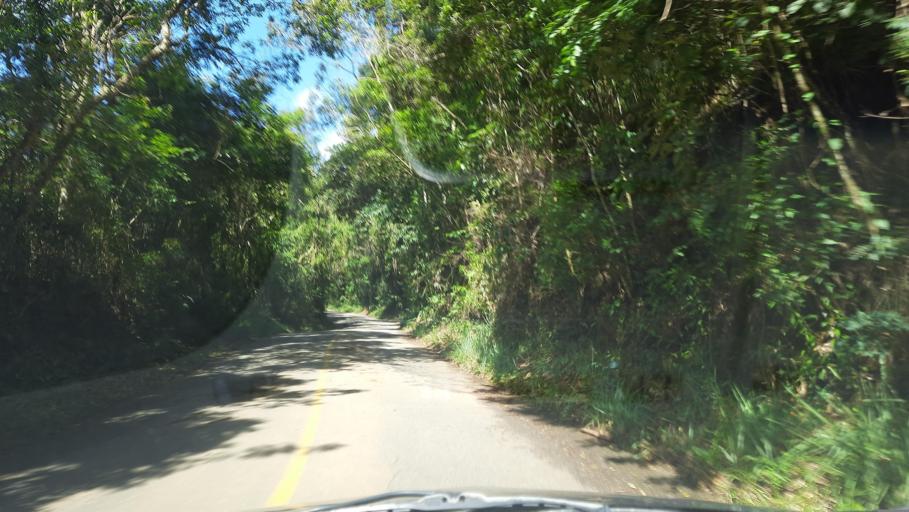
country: BR
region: Minas Gerais
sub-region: Pocos De Caldas
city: Pocos de Caldas
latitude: -21.7737
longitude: -46.5624
